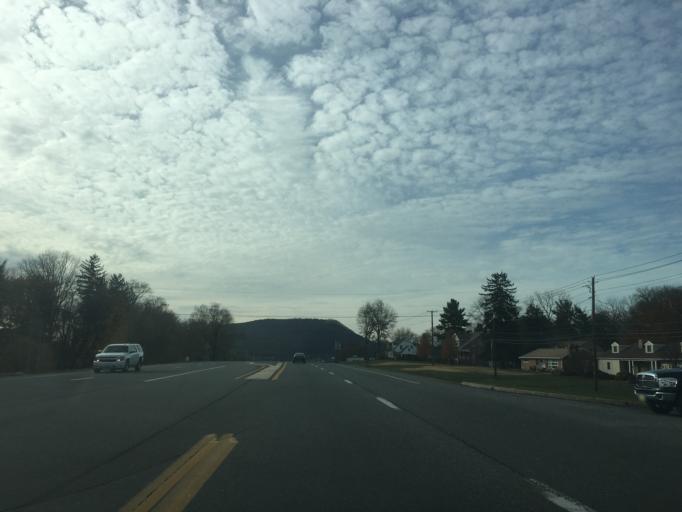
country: US
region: Pennsylvania
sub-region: Perry County
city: Marysville
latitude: 40.3264
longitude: -76.8856
